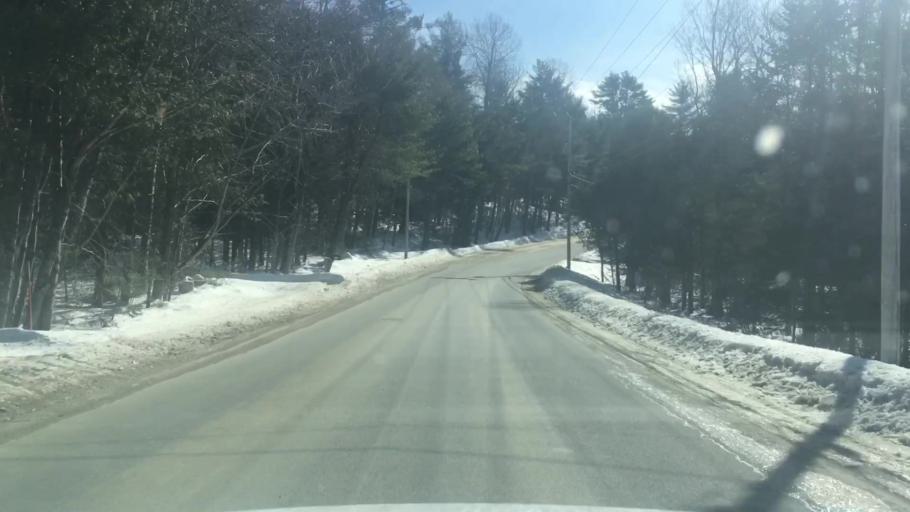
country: US
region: Maine
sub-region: Penobscot County
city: Holden
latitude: 44.7510
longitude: -68.6328
